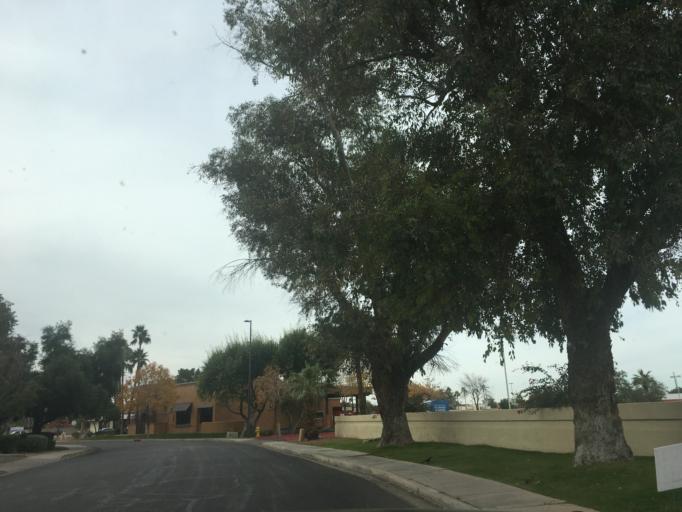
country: US
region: Arizona
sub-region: Maricopa County
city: Gilbert
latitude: 33.3612
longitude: -111.7886
